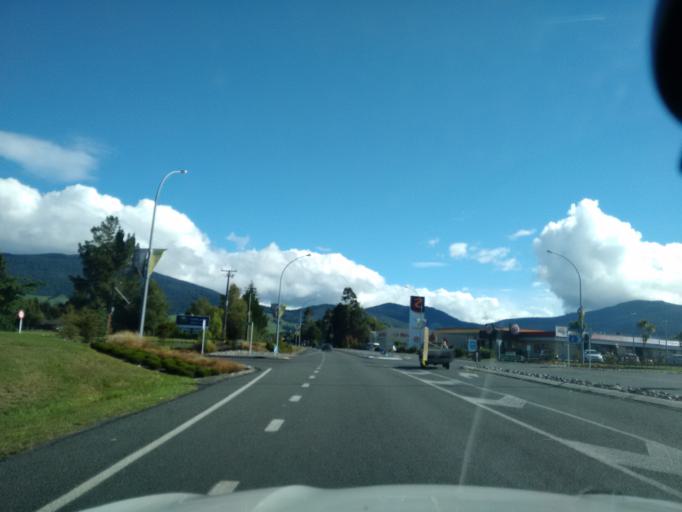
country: NZ
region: Waikato
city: Turangi
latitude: -38.9903
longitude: 175.8114
